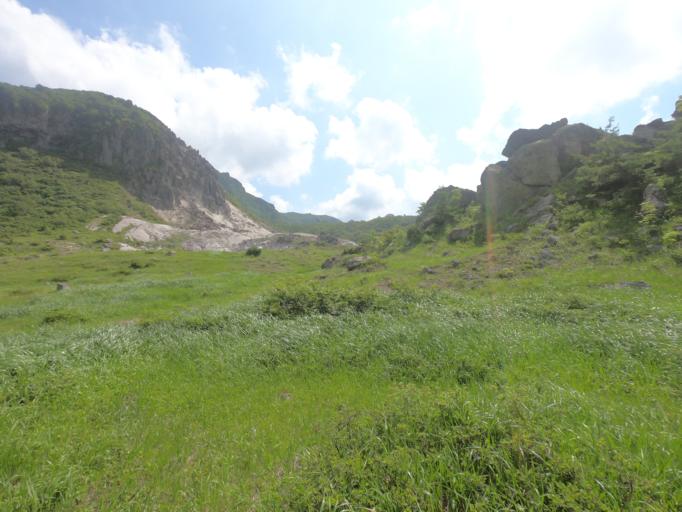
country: JP
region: Akita
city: Yuzawa
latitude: 38.9741
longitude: 140.7749
